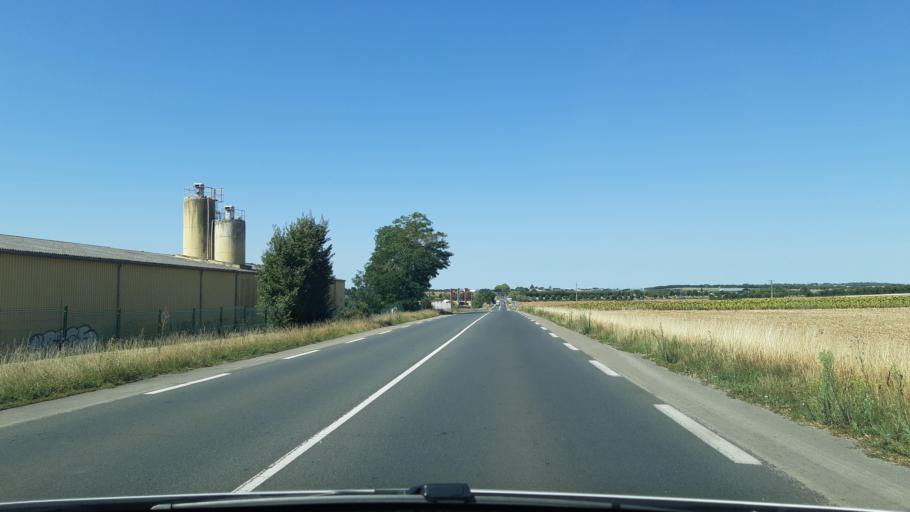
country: FR
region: Poitou-Charentes
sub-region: Departement des Deux-Sevres
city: La Creche
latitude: 46.3550
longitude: -0.3166
